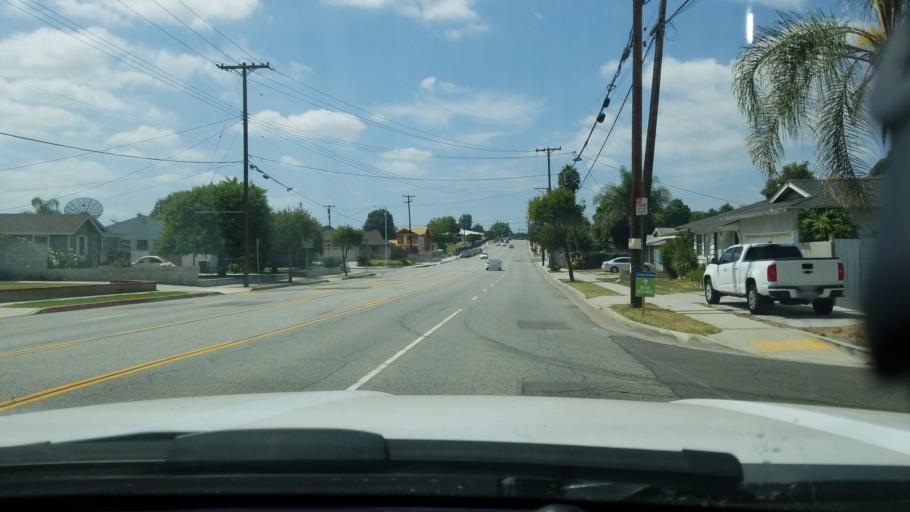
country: US
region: California
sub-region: Los Angeles County
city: South Whittier
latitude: 33.9398
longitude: -118.0345
